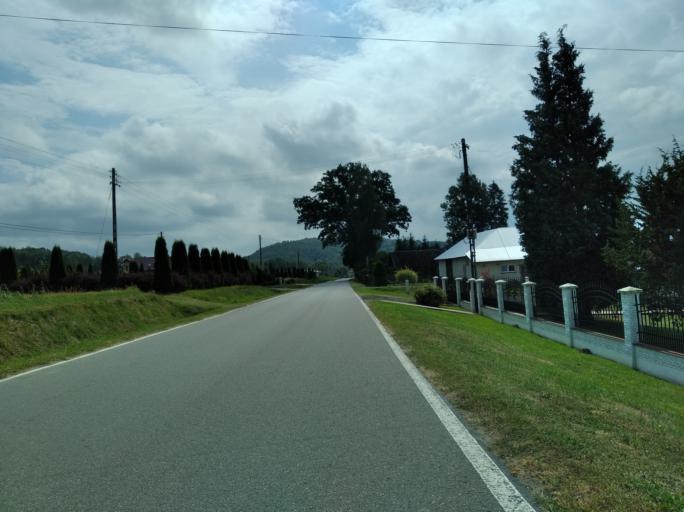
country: PL
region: Subcarpathian Voivodeship
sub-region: Powiat krosnienski
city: Wojaszowka
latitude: 49.7926
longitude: 21.6881
